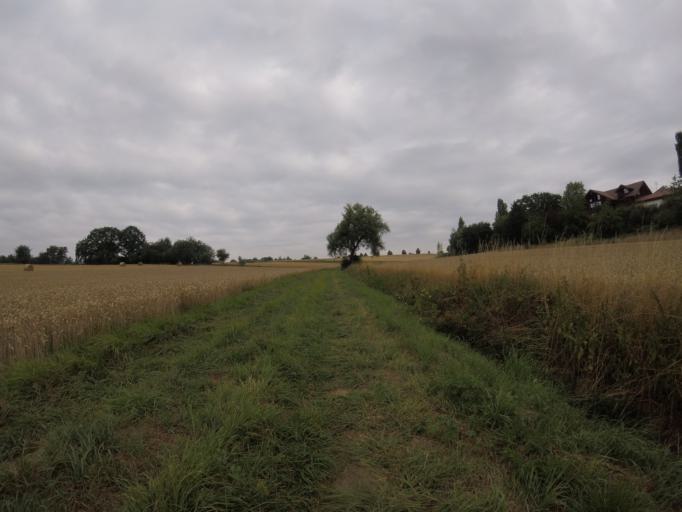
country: DE
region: Baden-Wuerttemberg
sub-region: Regierungsbezirk Stuttgart
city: Abstatt
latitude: 49.0749
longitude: 9.2988
